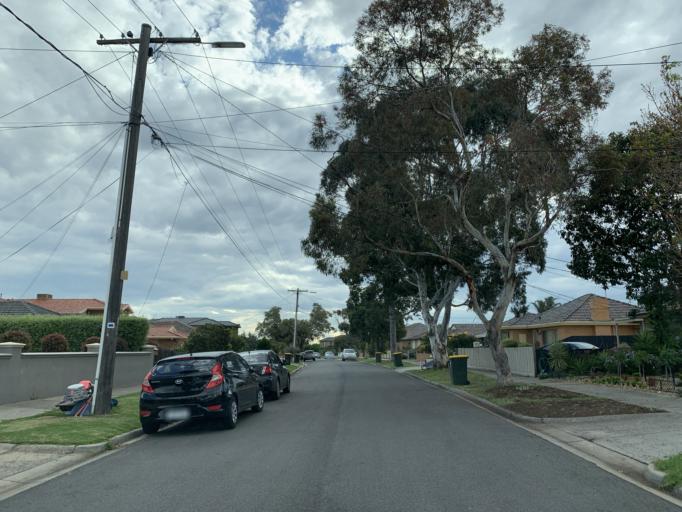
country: AU
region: Victoria
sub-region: Moonee Valley
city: Keilor East
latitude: -37.7516
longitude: 144.8574
